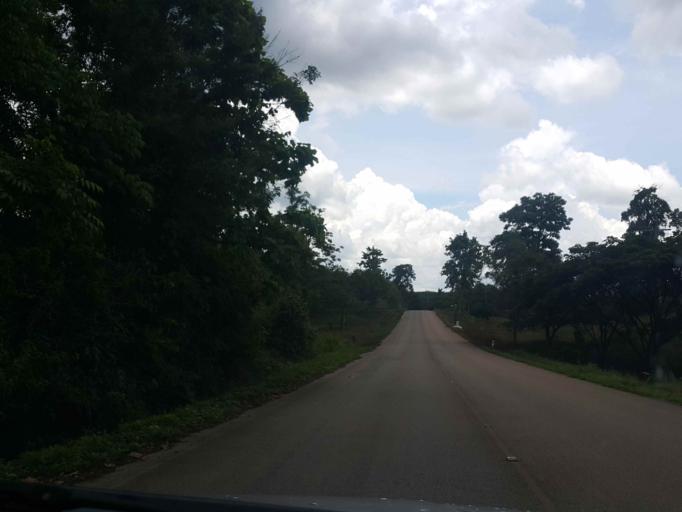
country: TH
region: Lampang
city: Ngao
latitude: 18.9552
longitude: 100.0748
